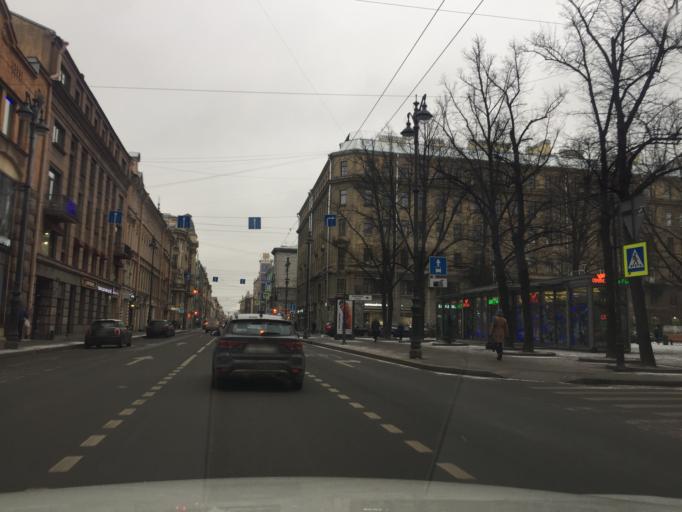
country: RU
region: St.-Petersburg
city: Petrogradka
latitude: 59.9627
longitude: 30.3070
